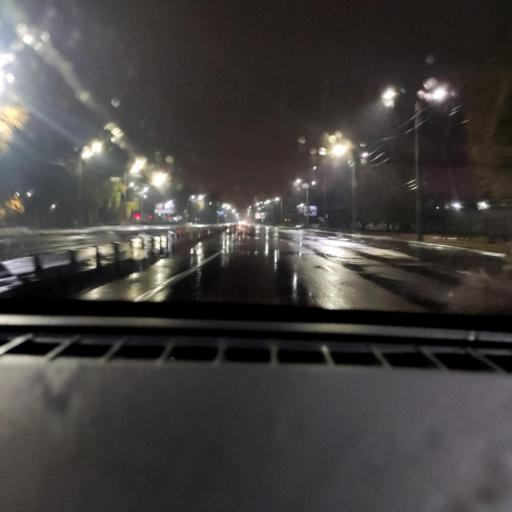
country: RU
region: Voronezj
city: Voronezh
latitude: 51.6537
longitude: 39.1736
